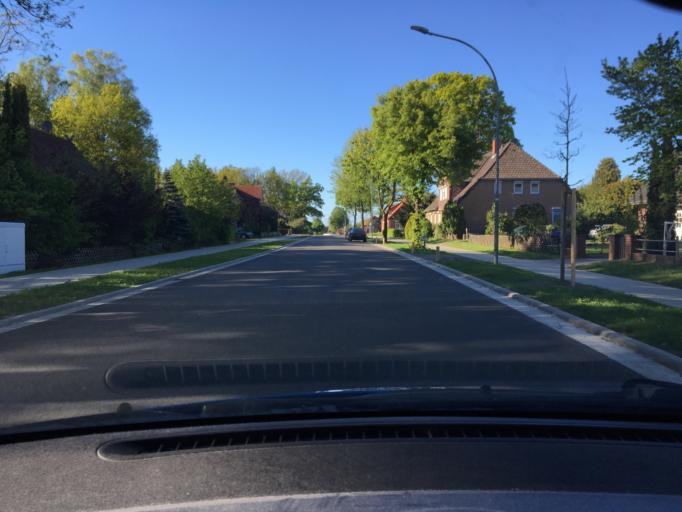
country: DE
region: Lower Saxony
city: Schneverdingen
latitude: 53.0735
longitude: 9.8634
